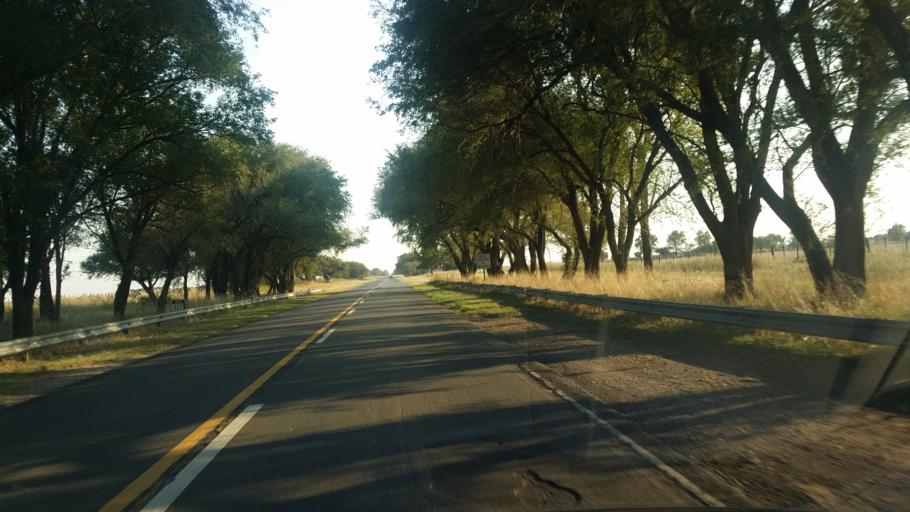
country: AR
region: La Pampa
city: Winifreda
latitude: -36.2146
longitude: -64.2782
